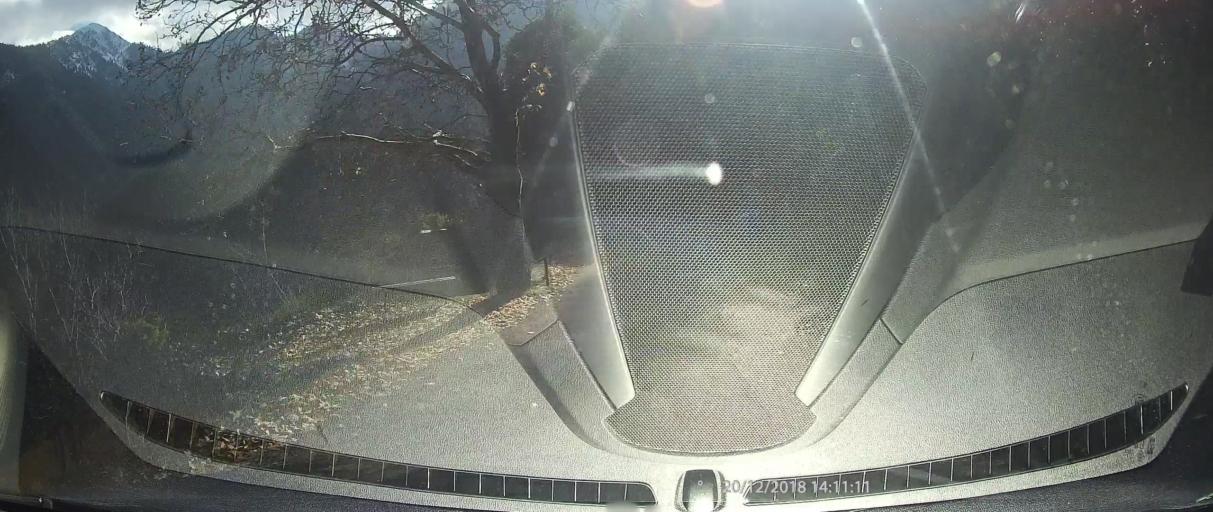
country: GR
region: West Greece
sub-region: Nomos Aitolias kai Akarnanias
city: Thermo
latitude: 38.7401
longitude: 21.6508
